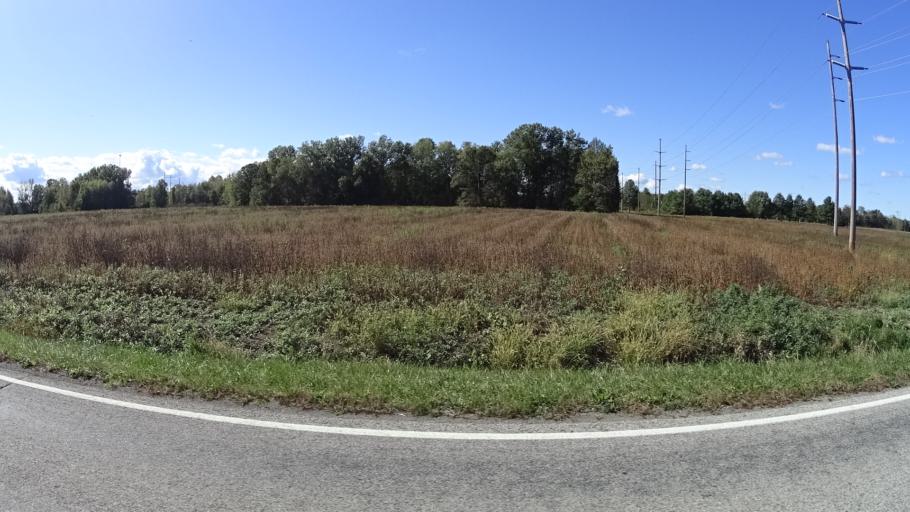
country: US
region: Ohio
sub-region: Lorain County
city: Grafton
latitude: 41.2989
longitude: -82.0859
